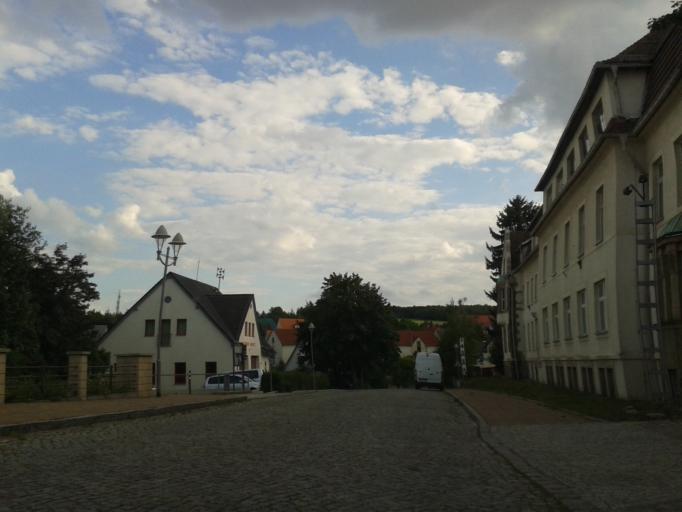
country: DE
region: Saxony
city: Bannewitz
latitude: 50.9940
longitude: 13.7223
